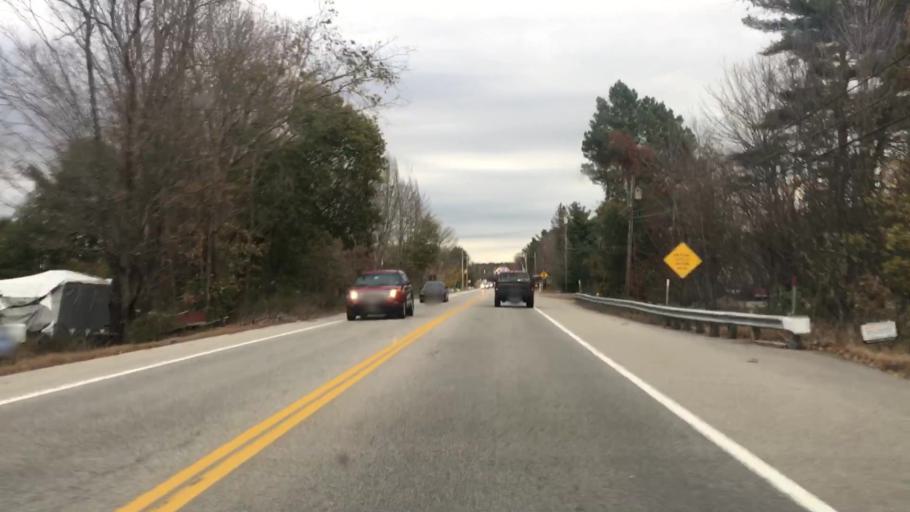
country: US
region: Maine
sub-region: York County
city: Alfred
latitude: 43.4728
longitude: -70.7160
